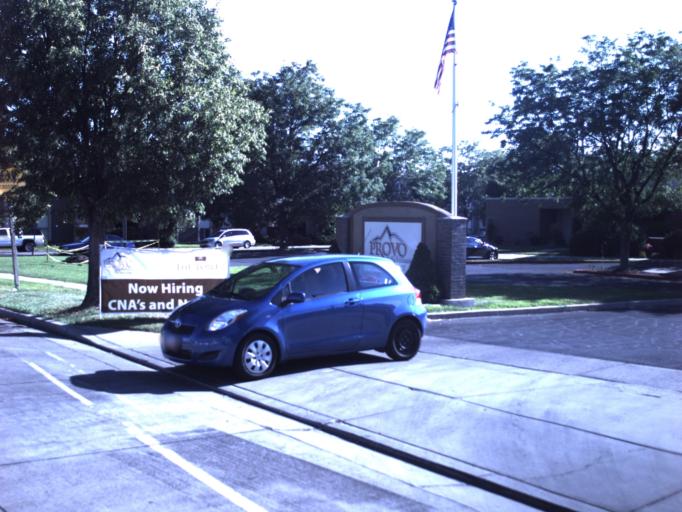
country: US
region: Utah
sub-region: Utah County
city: Provo
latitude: 40.2470
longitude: -111.6675
